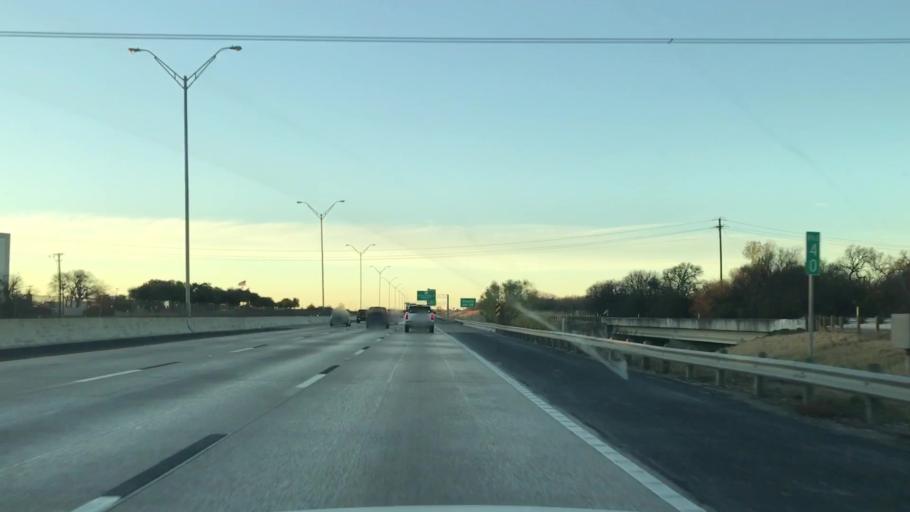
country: US
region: Texas
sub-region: Tarrant County
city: Crowley
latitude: 32.5900
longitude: -97.3200
